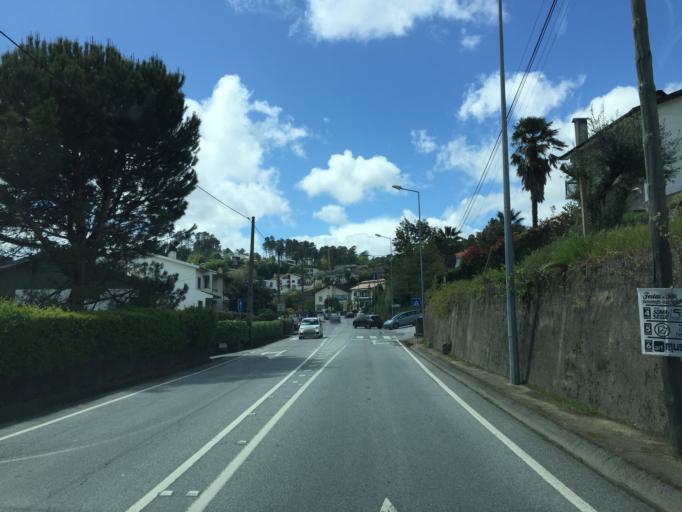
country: PT
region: Viseu
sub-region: Viseu
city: Viseu
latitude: 40.6546
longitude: -7.9425
